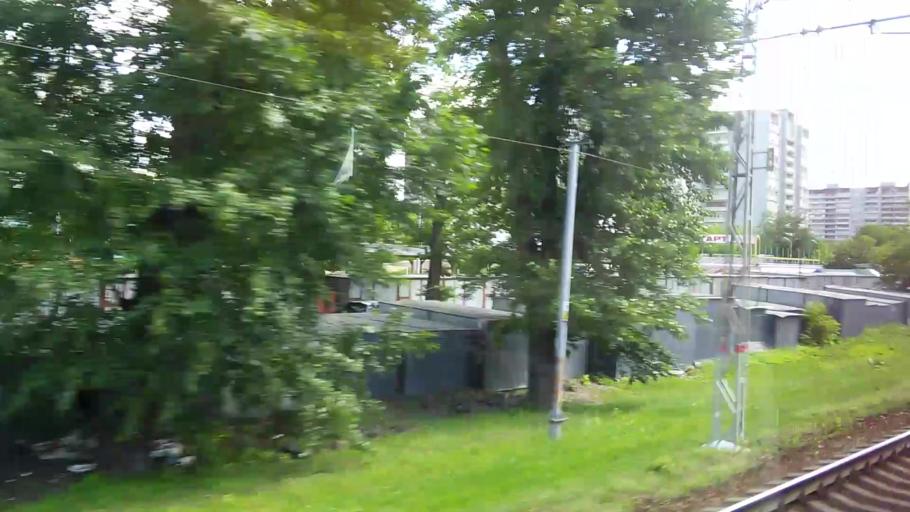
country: RU
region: Moscow
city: Likhobory
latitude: 55.8280
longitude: 37.5736
